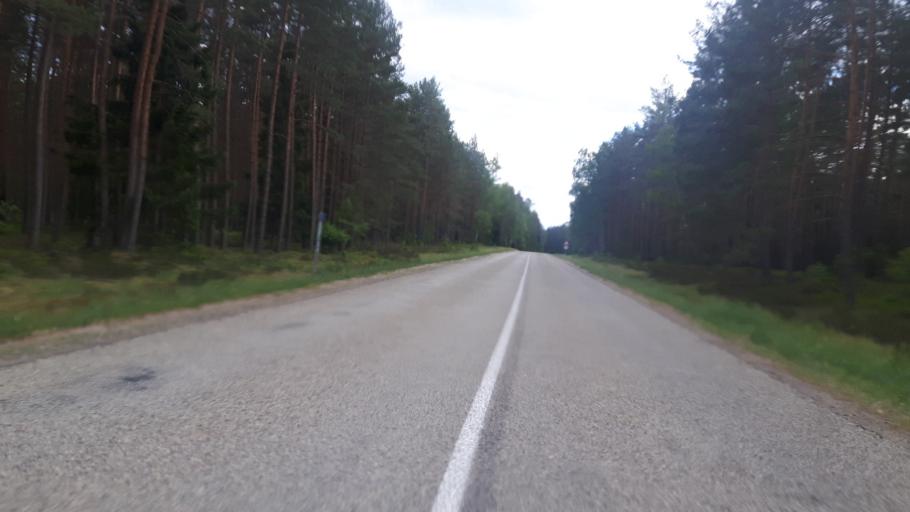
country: LV
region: Engure
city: Smarde
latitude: 57.0186
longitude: 23.3448
